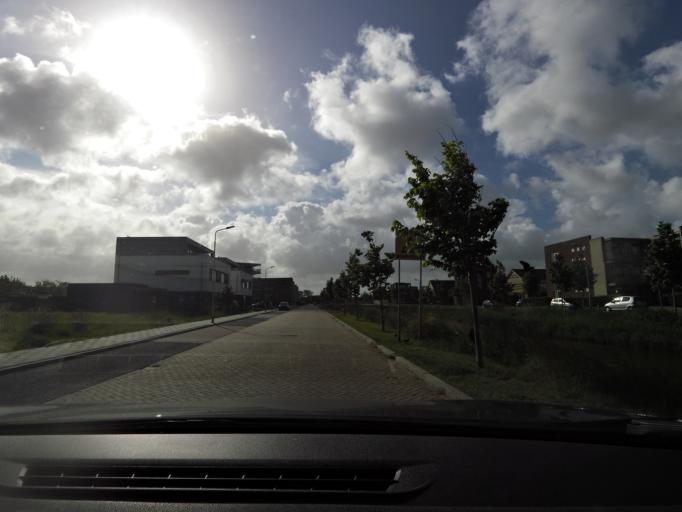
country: NL
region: Zeeland
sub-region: Schouwen-Duiveland
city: Scharendijke
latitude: 51.6442
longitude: 3.9030
